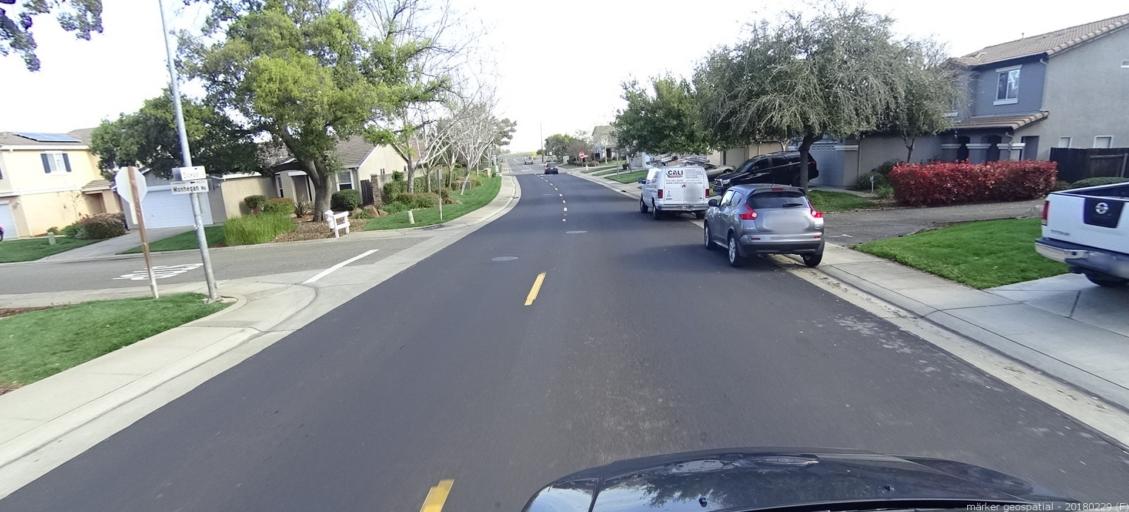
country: US
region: California
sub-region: Sacramento County
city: Rancho Cordova
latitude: 38.5482
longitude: -121.2814
